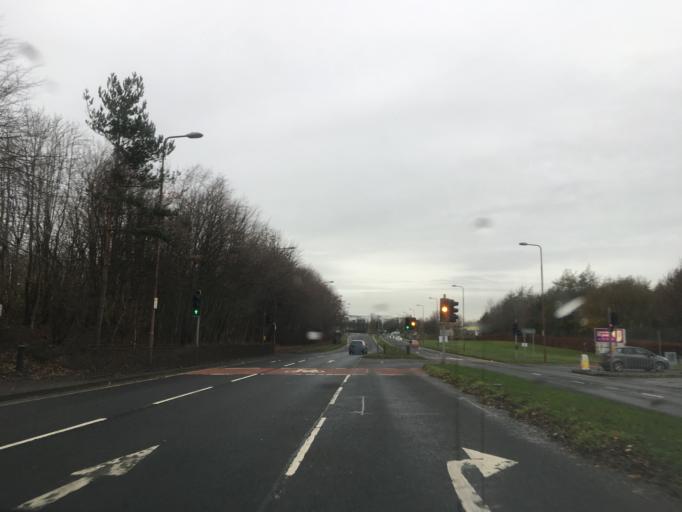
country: GB
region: Scotland
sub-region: Edinburgh
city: Currie
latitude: 55.9353
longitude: -3.3100
